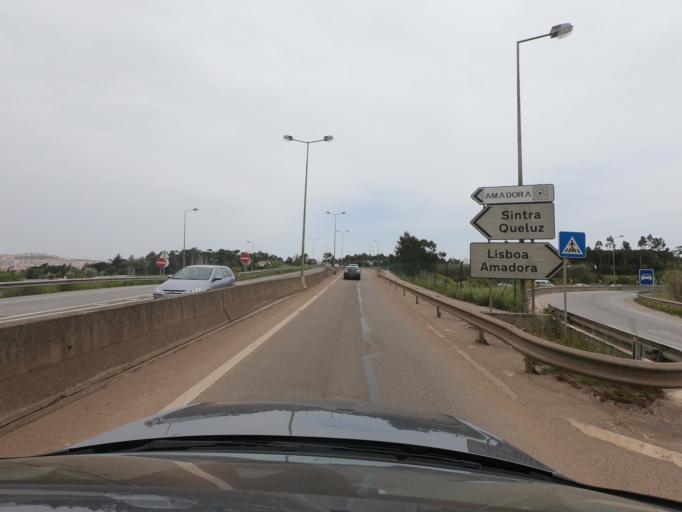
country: PT
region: Lisbon
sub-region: Sintra
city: Queluz
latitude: 38.7477
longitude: -9.2467
